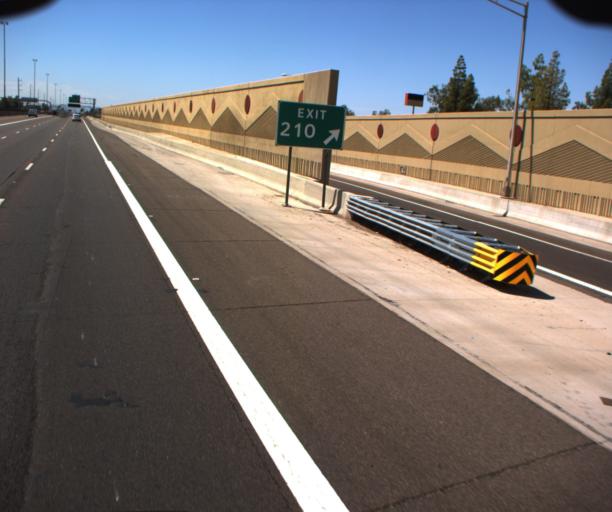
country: US
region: Arizona
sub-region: Maricopa County
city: Glendale
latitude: 33.6137
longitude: -112.1168
